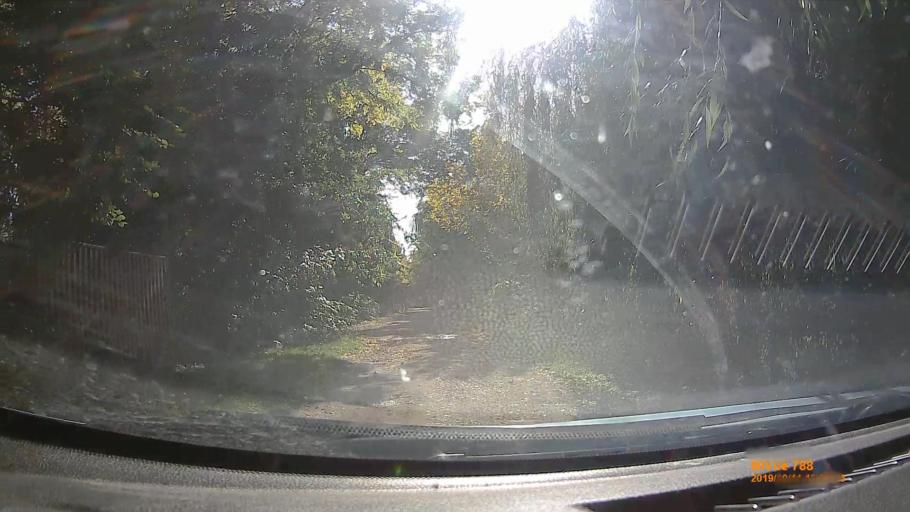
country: HU
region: Hajdu-Bihar
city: Balmazujvaros
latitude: 47.5405
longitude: 21.3266
